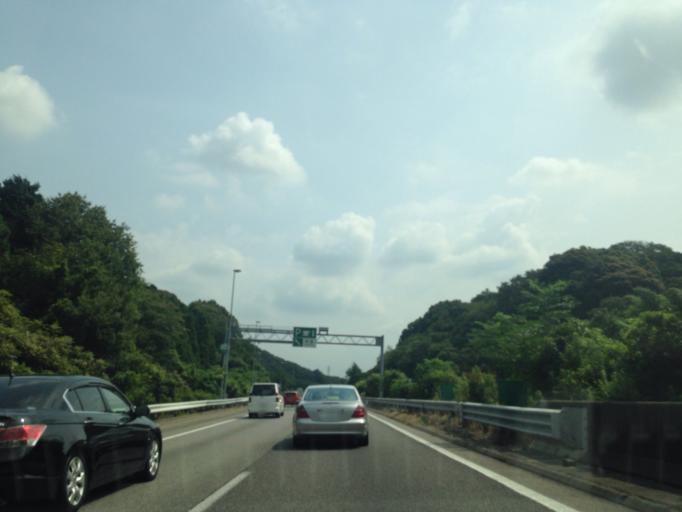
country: JP
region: Aichi
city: Kozakai-cho
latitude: 34.8484
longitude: 137.3577
